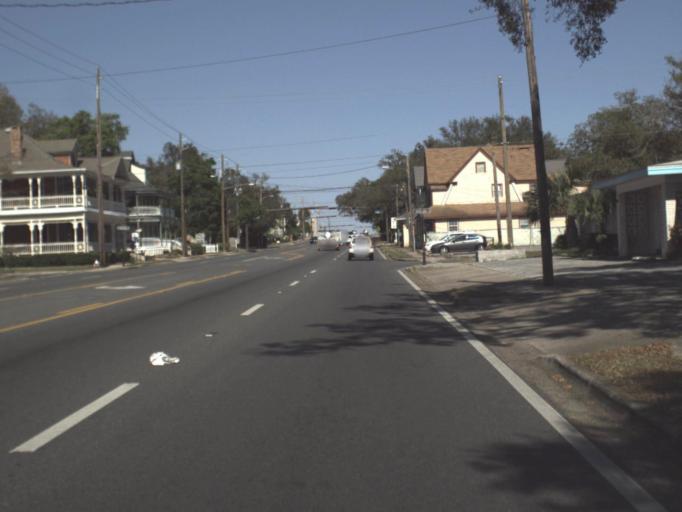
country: US
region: Florida
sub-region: Escambia County
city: Pensacola
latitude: 30.4205
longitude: -87.2219
